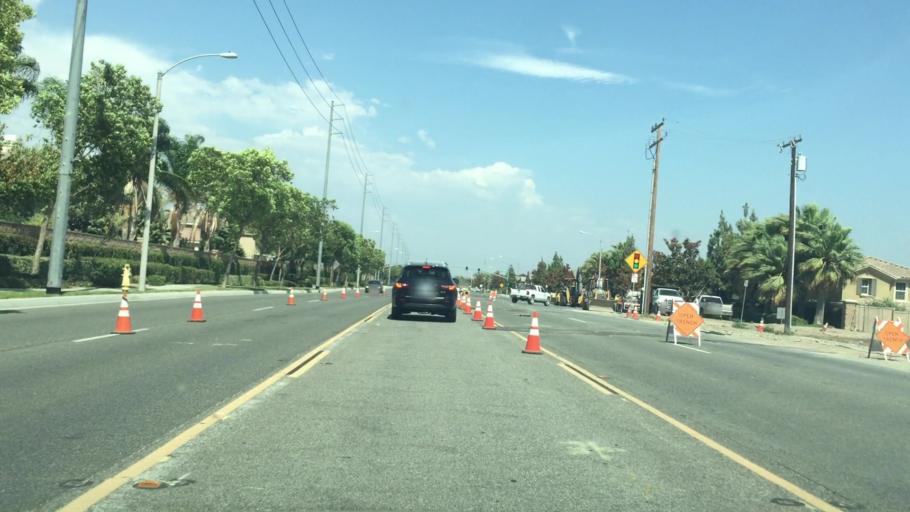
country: US
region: California
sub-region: Riverside County
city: Norco
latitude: 33.9609
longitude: -117.6002
